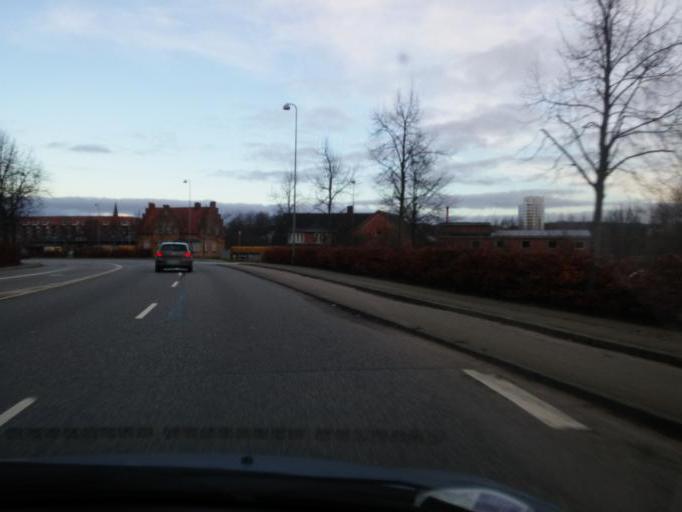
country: DK
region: South Denmark
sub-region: Vejle Kommune
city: Vejle
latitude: 55.7010
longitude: 9.5359
